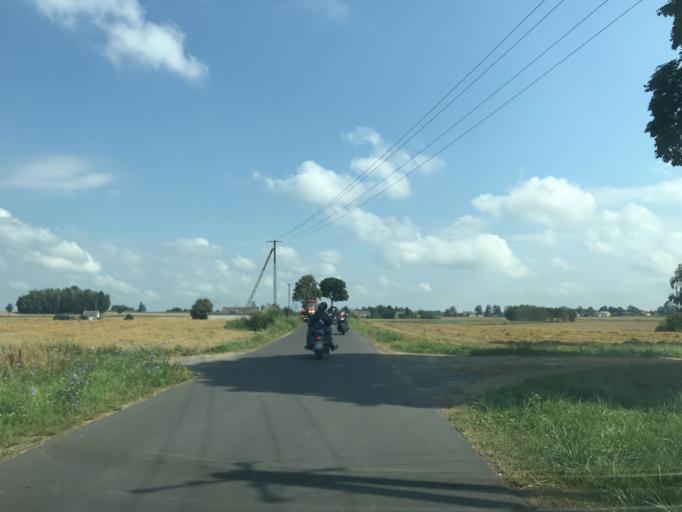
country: PL
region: Warmian-Masurian Voivodeship
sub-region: Powiat nowomiejski
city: Biskupiec
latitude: 53.4586
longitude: 19.4601
